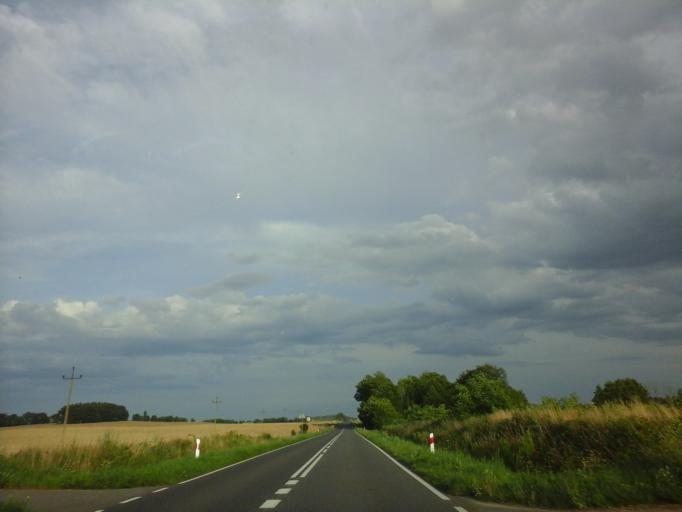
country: PL
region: West Pomeranian Voivodeship
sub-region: Powiat kamienski
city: Golczewo
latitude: 53.8621
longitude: 14.9200
